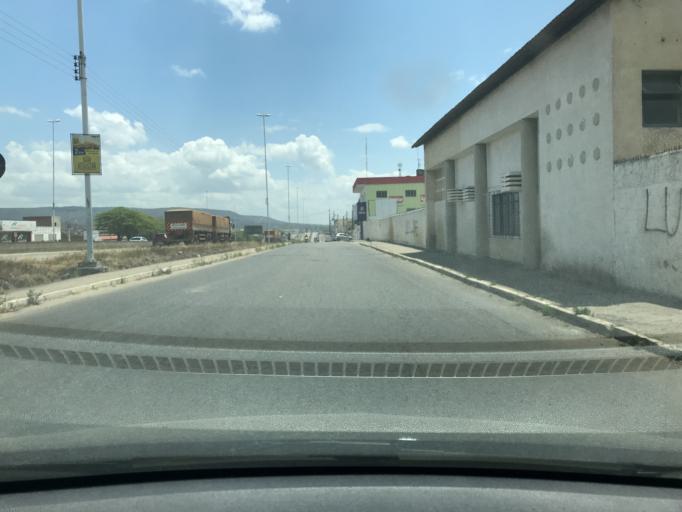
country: BR
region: Pernambuco
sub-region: Bezerros
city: Bezerros
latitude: -8.2410
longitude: -35.7499
